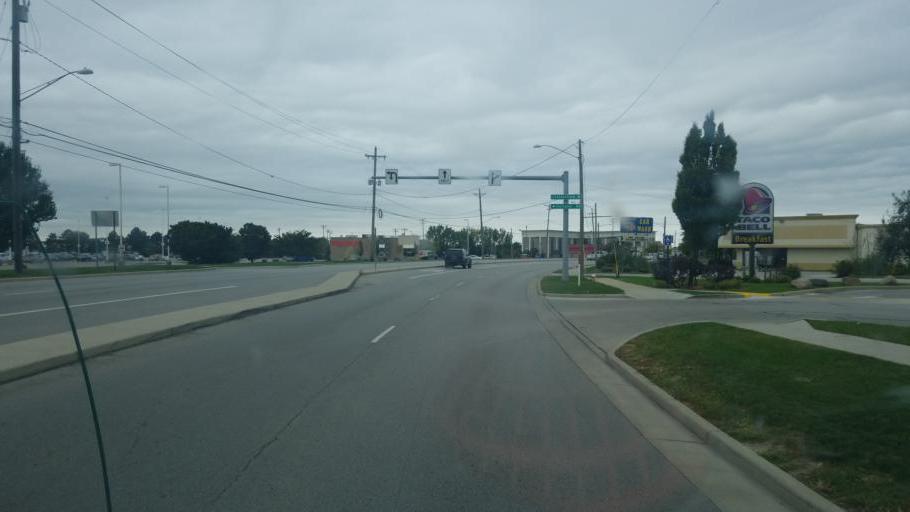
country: US
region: Ohio
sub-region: Lucas County
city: Maumee
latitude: 41.5794
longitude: -83.6640
